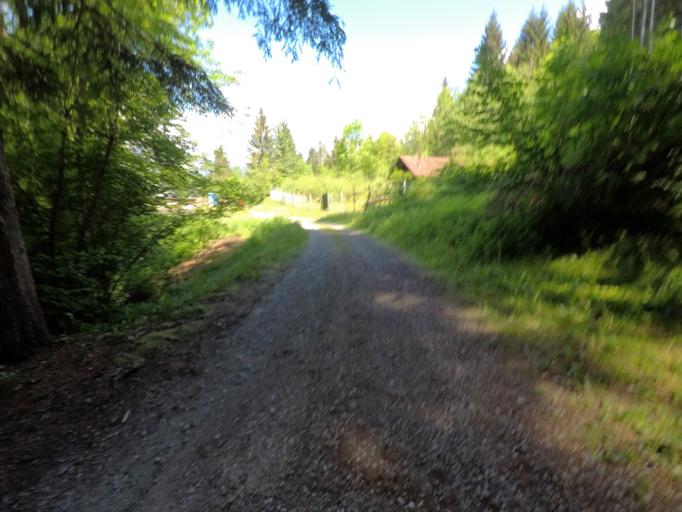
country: IT
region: Friuli Venezia Giulia
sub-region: Provincia di Udine
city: Ovaro
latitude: 46.4777
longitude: 12.8715
